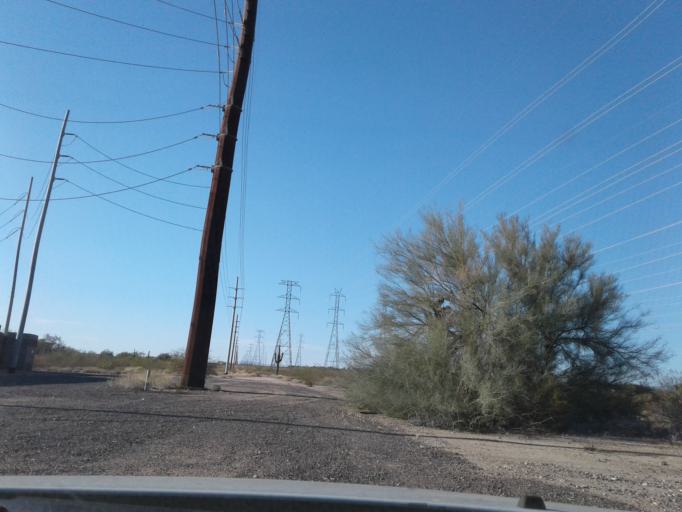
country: US
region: Arizona
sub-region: Maricopa County
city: Paradise Valley
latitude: 33.6521
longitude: -111.8921
